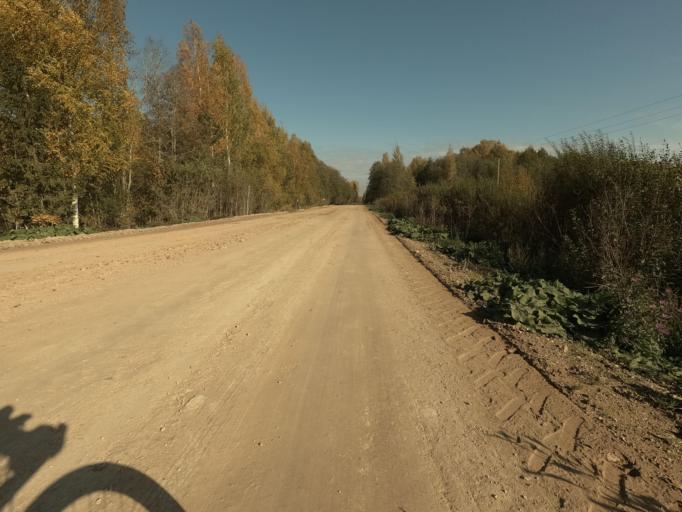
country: RU
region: Novgorod
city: Batetskiy
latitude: 58.8255
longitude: 30.7086
